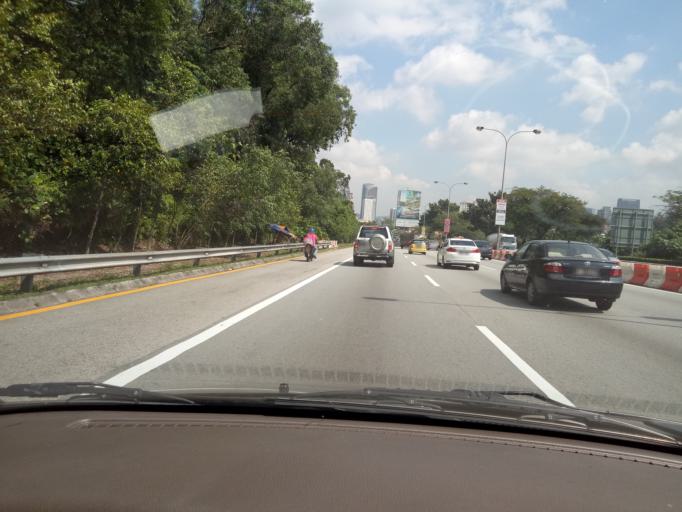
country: MY
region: Kuala Lumpur
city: Kuala Lumpur
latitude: 3.1104
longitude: 101.6893
